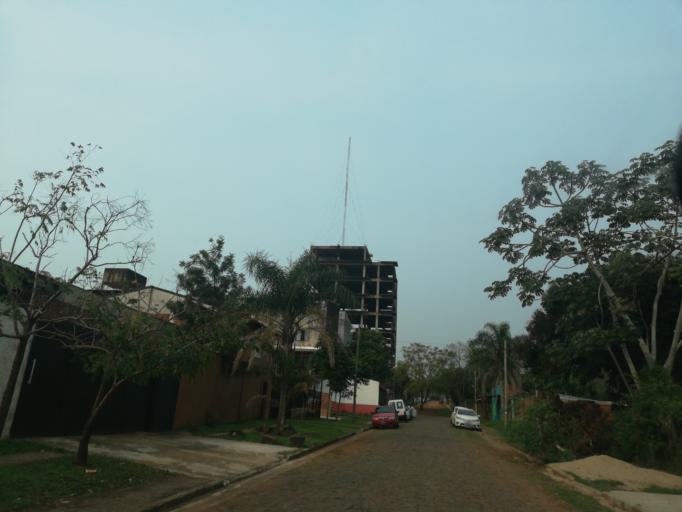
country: AR
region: Misiones
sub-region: Departamento de Capital
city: Posadas
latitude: -27.3722
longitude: -55.9334
